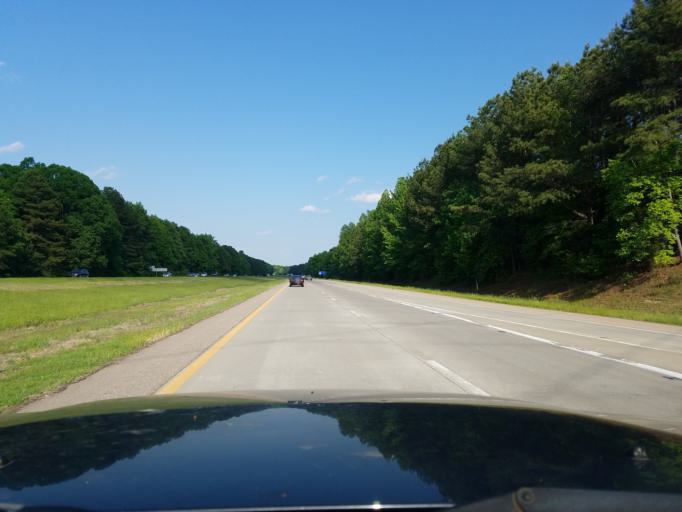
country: US
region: North Carolina
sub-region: Vance County
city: South Henderson
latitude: 36.3204
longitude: -78.4858
